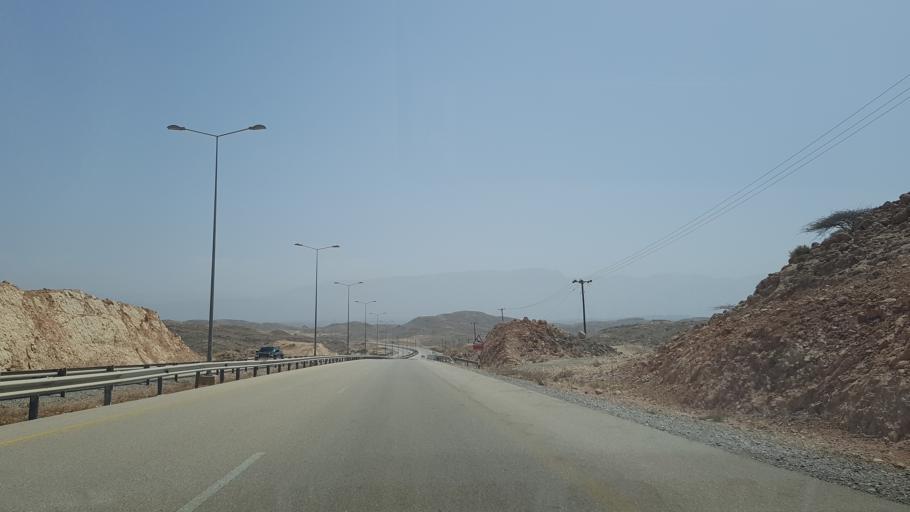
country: OM
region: Muhafazat Masqat
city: Muscat
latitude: 23.1702
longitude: 58.9772
